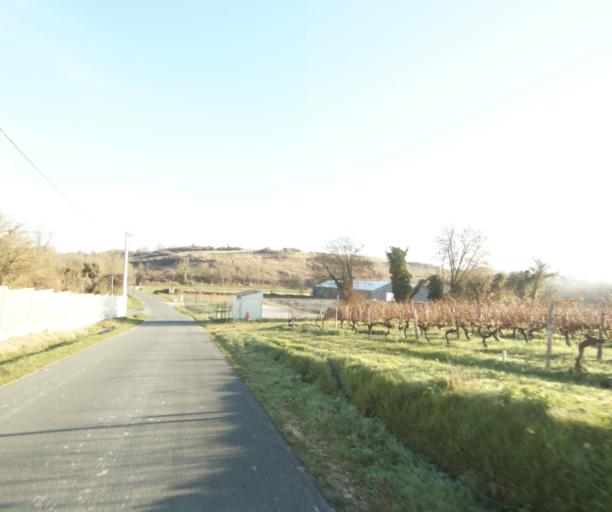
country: FR
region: Poitou-Charentes
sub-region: Departement de la Charente-Maritime
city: Cherac
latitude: 45.7036
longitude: -0.4335
